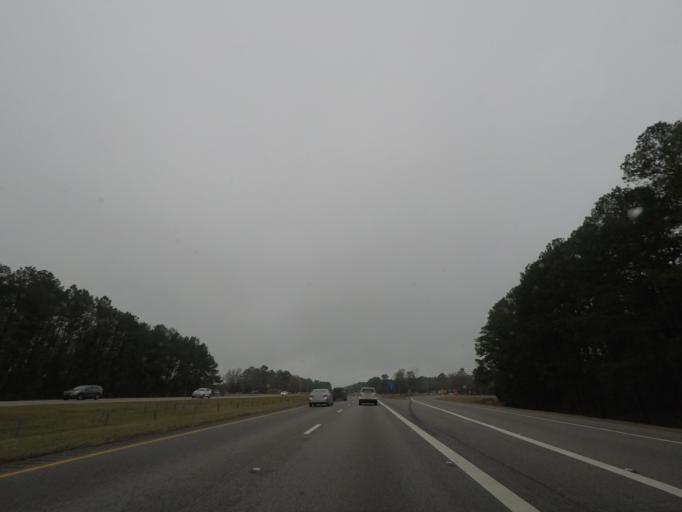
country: US
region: South Carolina
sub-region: Florence County
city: Timmonsville
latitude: 33.9505
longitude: -80.0546
